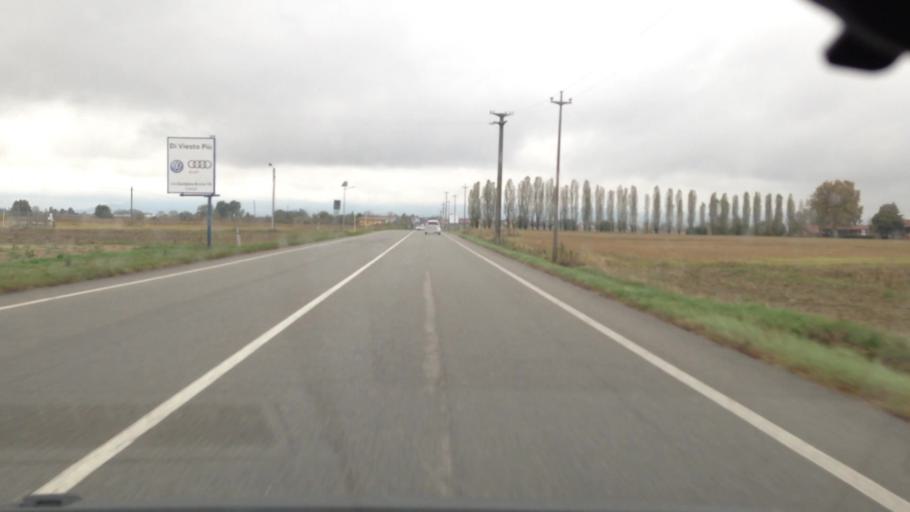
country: IT
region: Piedmont
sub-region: Provincia di Torino
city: Riva Presso Chieri
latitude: 44.9696
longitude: 7.8951
